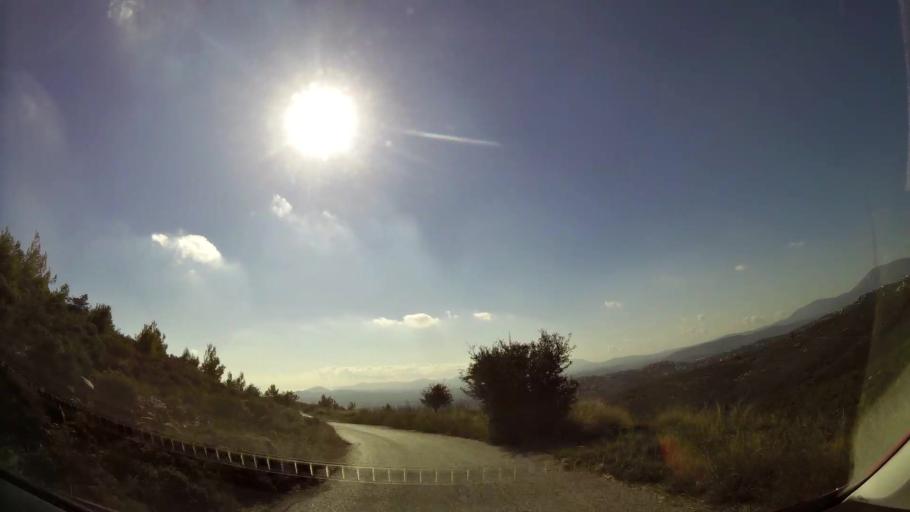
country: GR
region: Attica
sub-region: Nomarchia Anatolikis Attikis
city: Dhrafi
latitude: 38.0401
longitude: 23.9191
